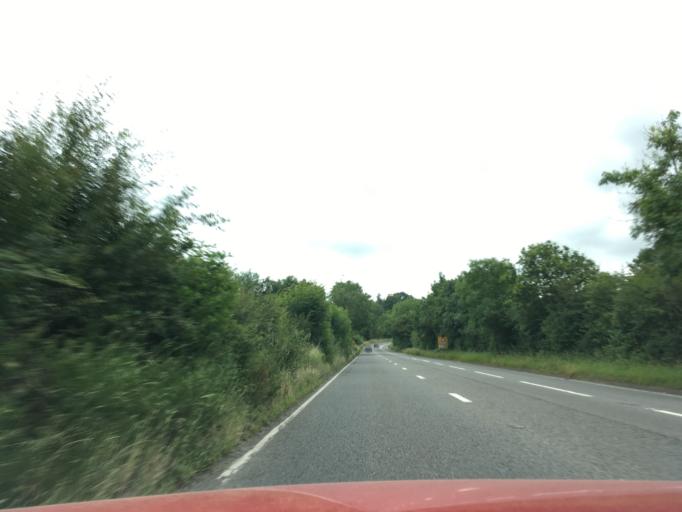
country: GB
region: England
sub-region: Gloucestershire
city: Charlton Kings
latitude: 51.8815
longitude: -2.0015
